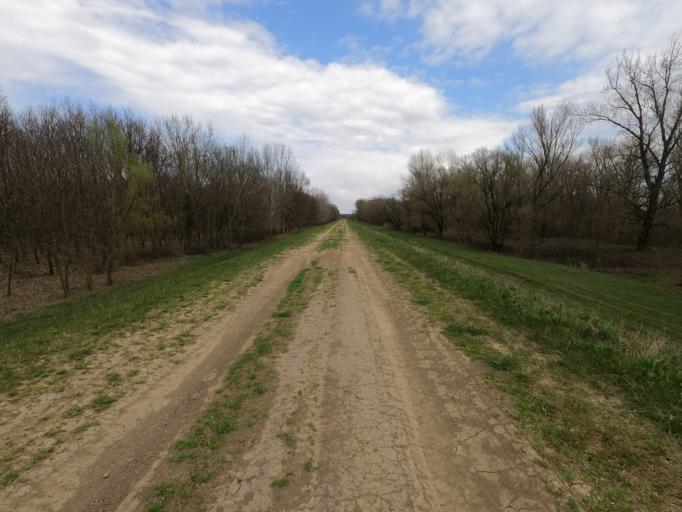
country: HU
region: Jasz-Nagykun-Szolnok
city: Turkeve
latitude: 47.0874
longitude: 20.7676
